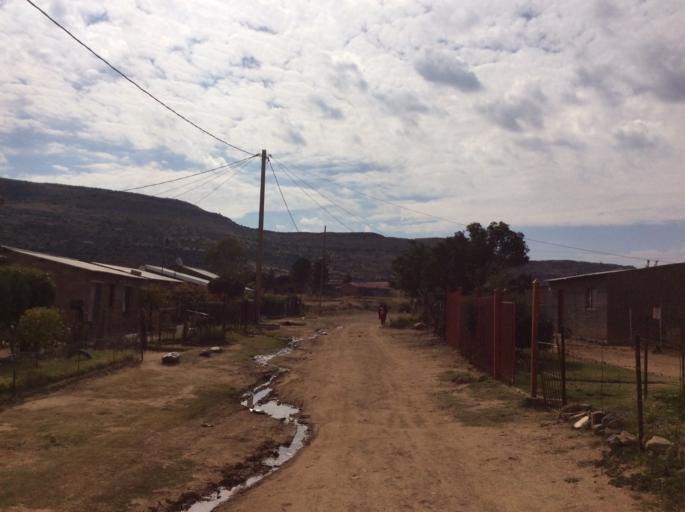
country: LS
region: Mafeteng
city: Mafeteng
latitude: -29.7208
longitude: 27.0253
